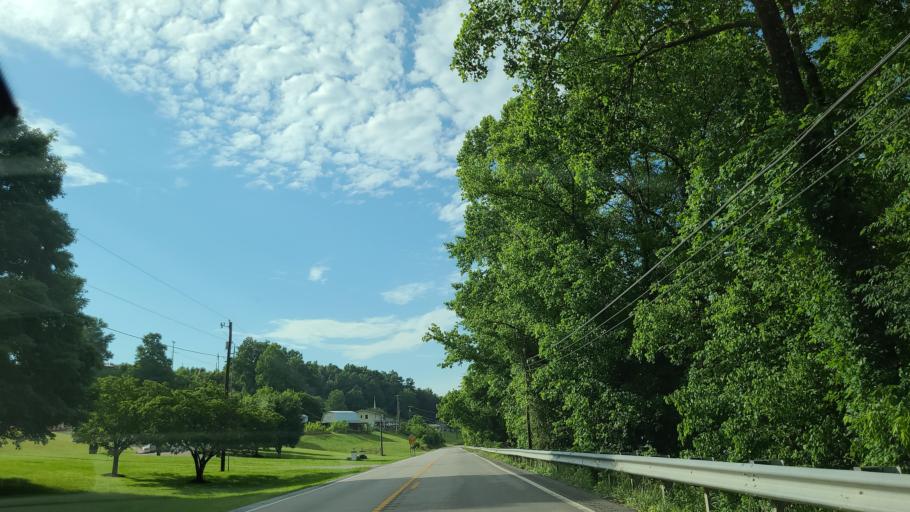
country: US
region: Kentucky
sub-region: Whitley County
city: Williamsburg
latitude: 36.7433
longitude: -84.1361
